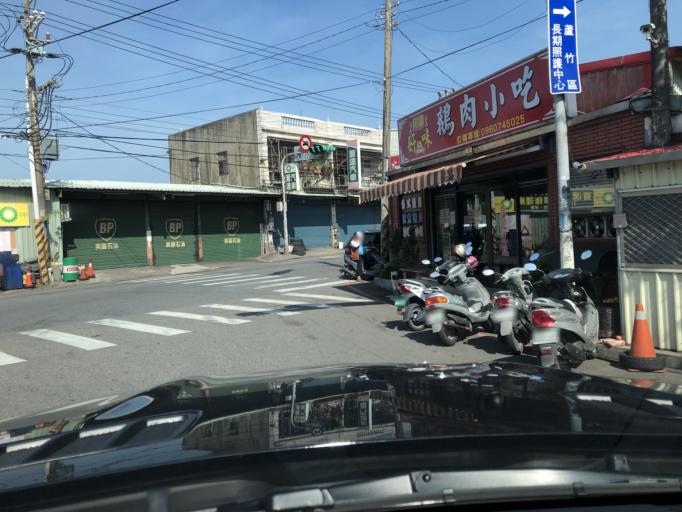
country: TW
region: Taiwan
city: Taoyuan City
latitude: 25.0851
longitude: 121.2876
